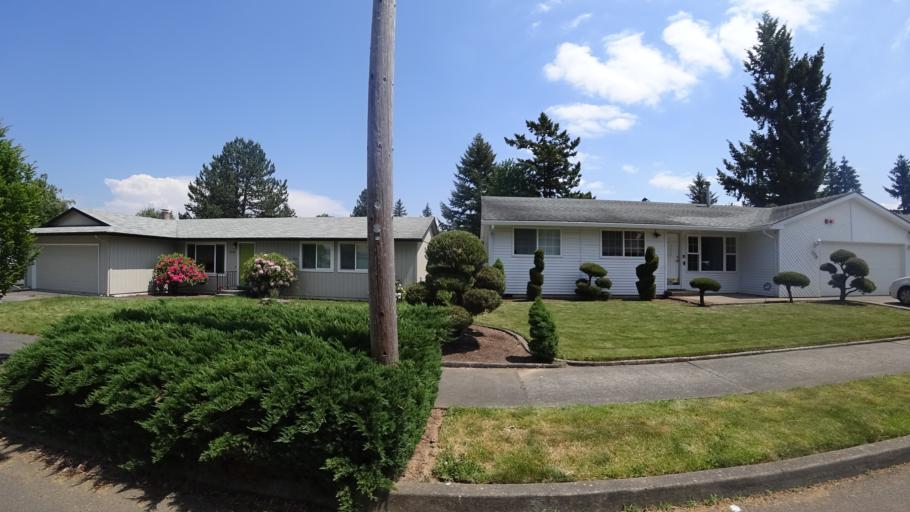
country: US
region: Oregon
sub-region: Multnomah County
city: Fairview
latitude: 45.5401
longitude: -122.4980
